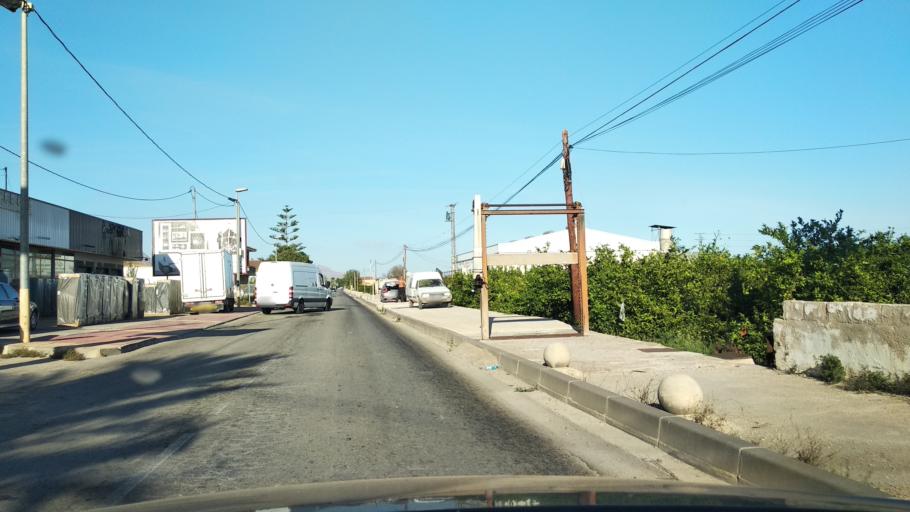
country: ES
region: Murcia
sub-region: Murcia
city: Santomera
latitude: 38.0401
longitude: -1.0475
